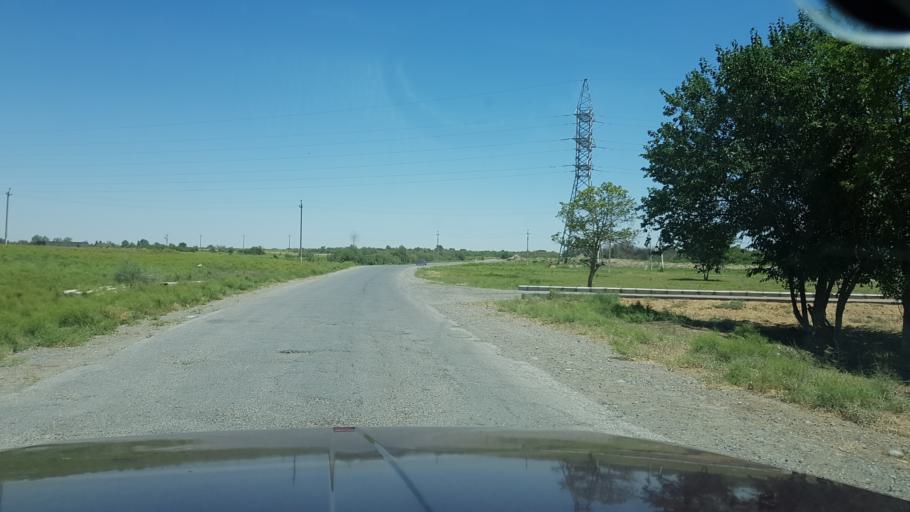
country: TM
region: Ahal
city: Annau
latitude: 37.8845
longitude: 58.7320
